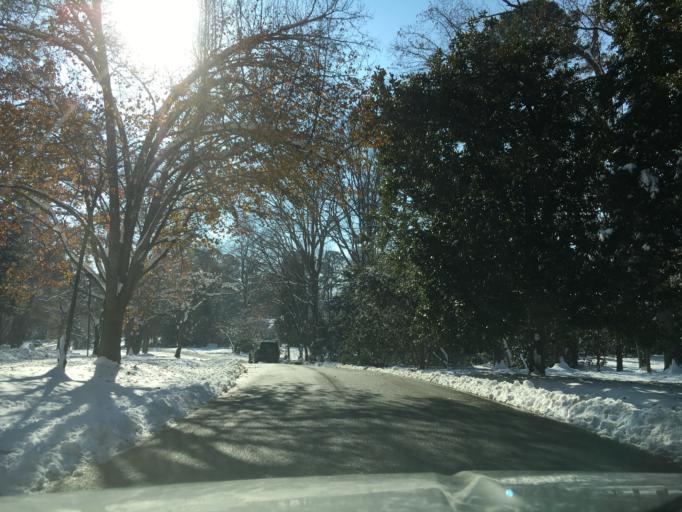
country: US
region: Virginia
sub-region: Henrico County
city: Tuckahoe
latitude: 37.5794
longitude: -77.5503
